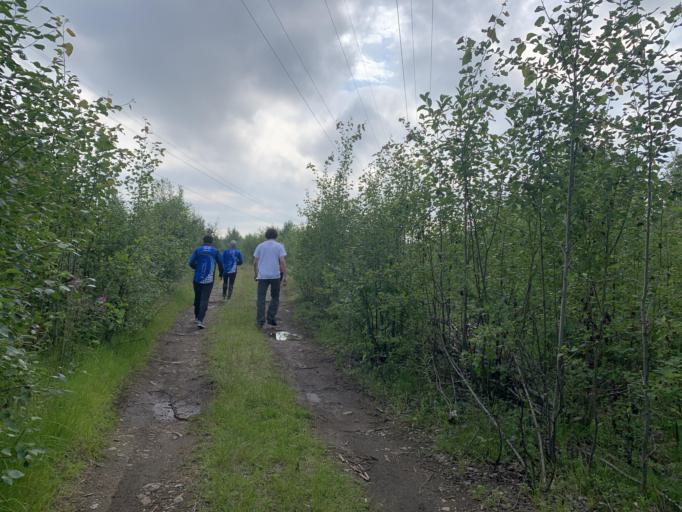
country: RU
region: Murmansk
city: Monchegorsk
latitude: 67.7970
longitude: 32.7905
